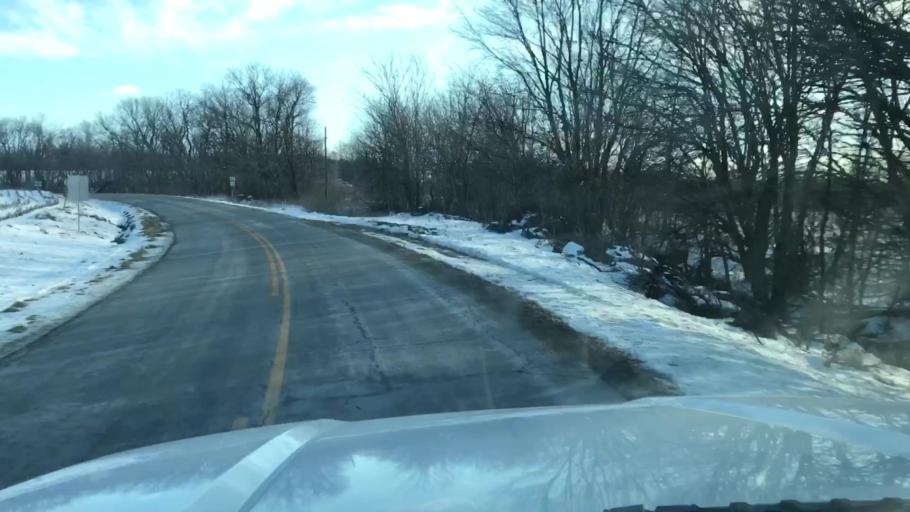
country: US
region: Missouri
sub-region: Holt County
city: Oregon
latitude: 40.1031
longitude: -95.0226
